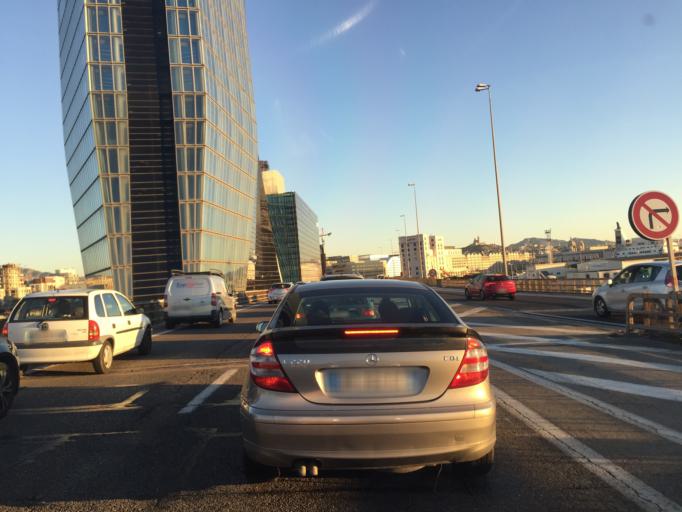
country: FR
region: Provence-Alpes-Cote d'Azur
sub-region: Departement des Bouches-du-Rhone
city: Marseille 03
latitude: 43.3159
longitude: 5.3649
